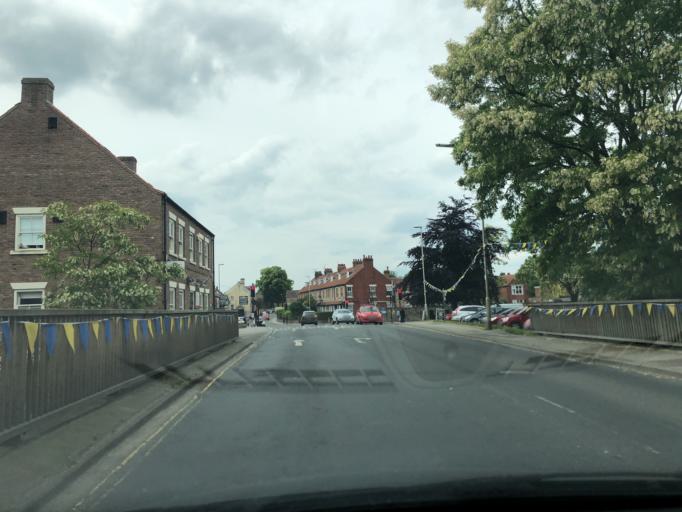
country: GB
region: England
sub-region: North Yorkshire
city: Pickering
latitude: 54.2448
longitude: -0.7786
